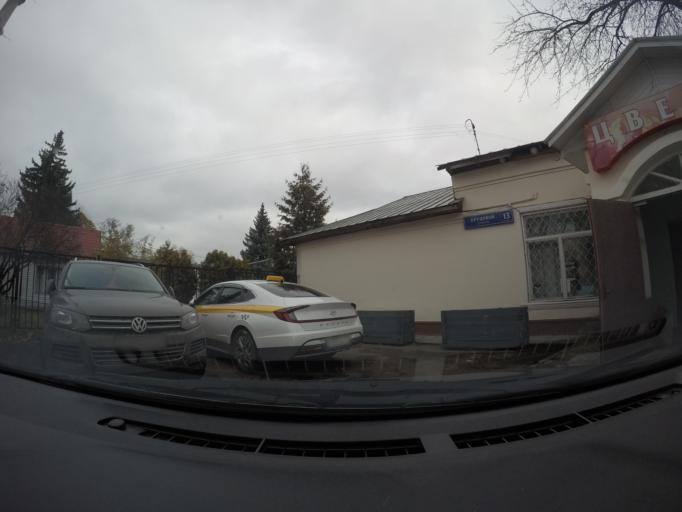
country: RU
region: Moscow
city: Ostankinskiy
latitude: 55.8174
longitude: 37.6137
